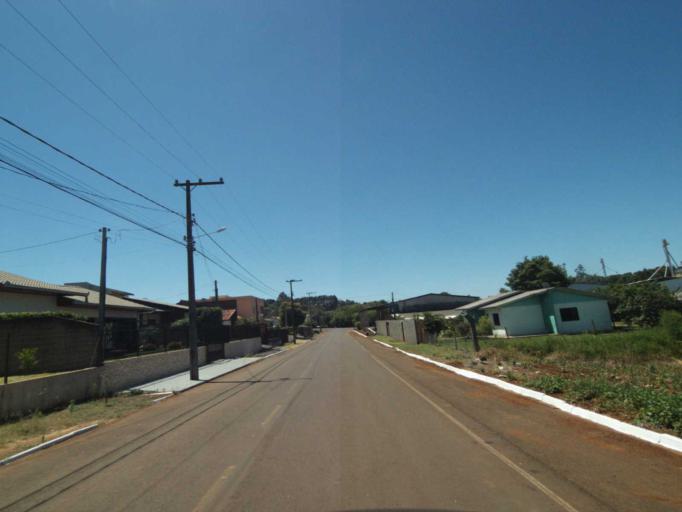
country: BR
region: Parana
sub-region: Coronel Vivida
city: Coronel Vivida
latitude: -25.9797
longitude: -52.8151
